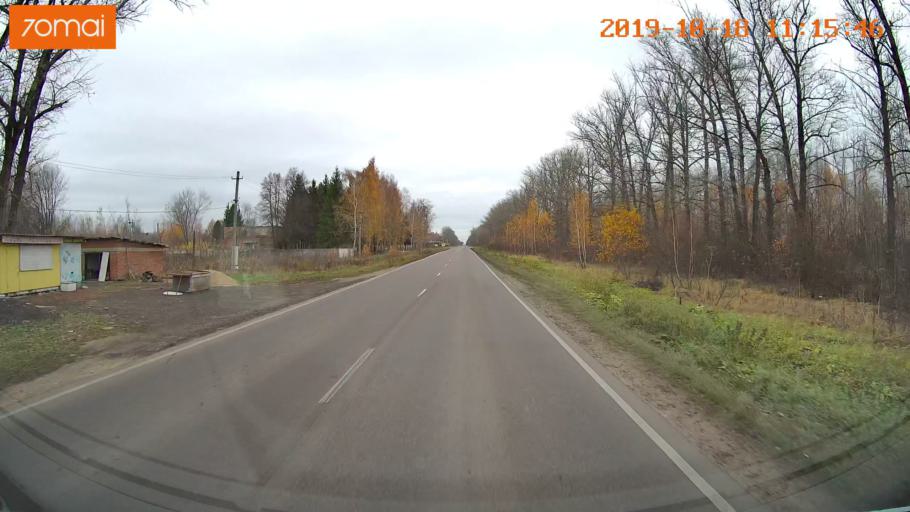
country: RU
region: Tula
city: Kimovsk
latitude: 53.9971
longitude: 38.5478
